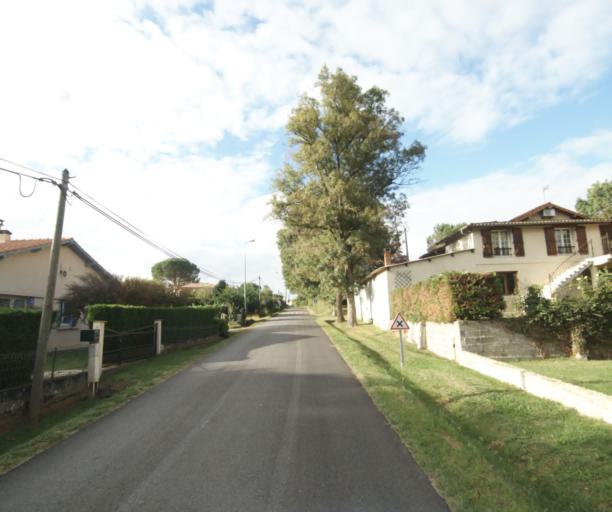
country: FR
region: Midi-Pyrenees
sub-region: Departement du Gers
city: Eauze
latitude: 43.8661
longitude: 0.0975
